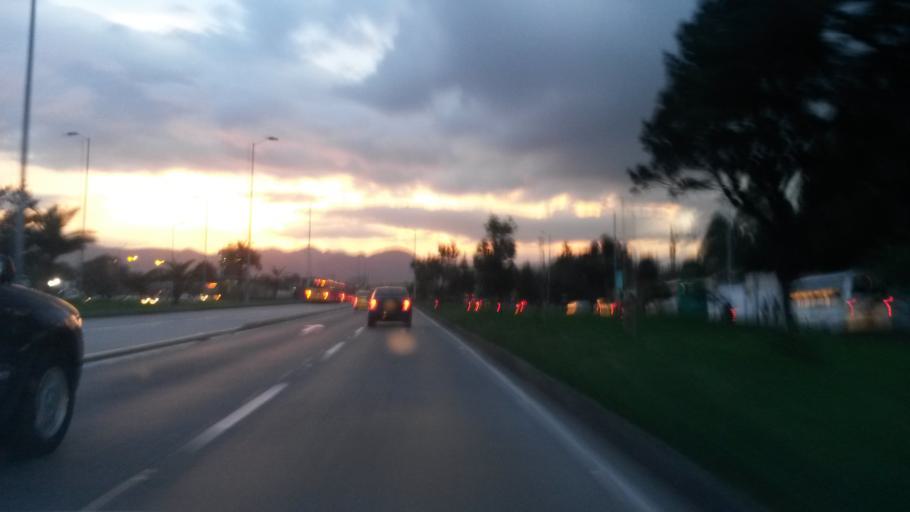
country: CO
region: Bogota D.C.
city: Bogota
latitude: 4.6763
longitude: -74.1182
